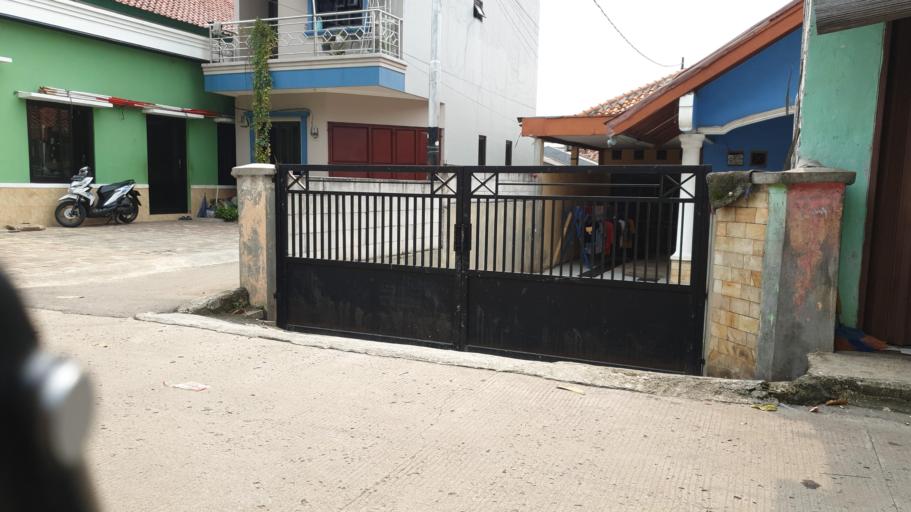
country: ID
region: West Java
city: Depok
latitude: -6.3313
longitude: 106.8231
